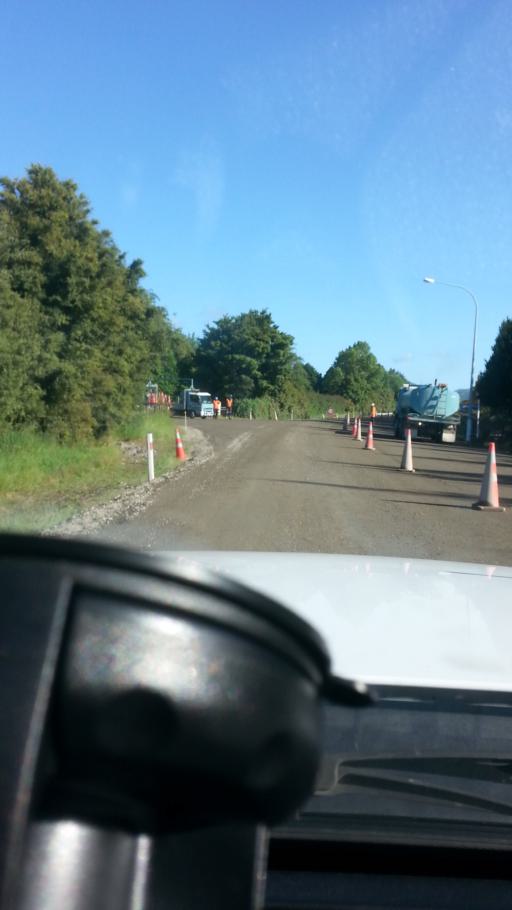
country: NZ
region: Wellington
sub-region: Masterton District
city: Masterton
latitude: -40.8099
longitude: 175.6206
